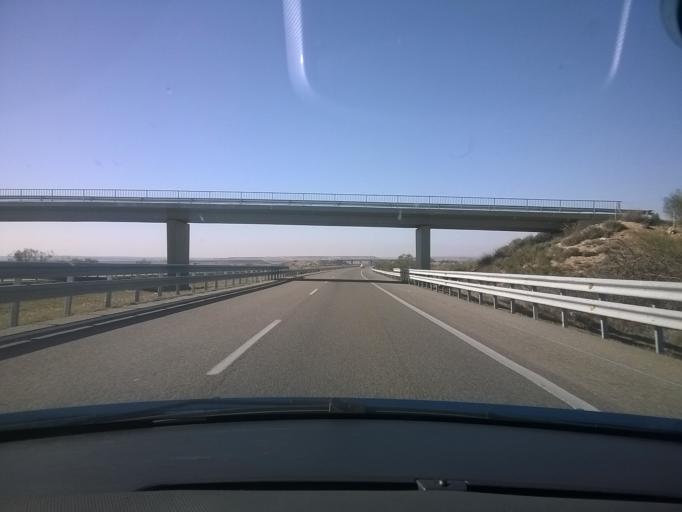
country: ES
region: Aragon
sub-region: Provincia de Zaragoza
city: Mequinensa / Mequinenza
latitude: 41.4690
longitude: 0.2268
